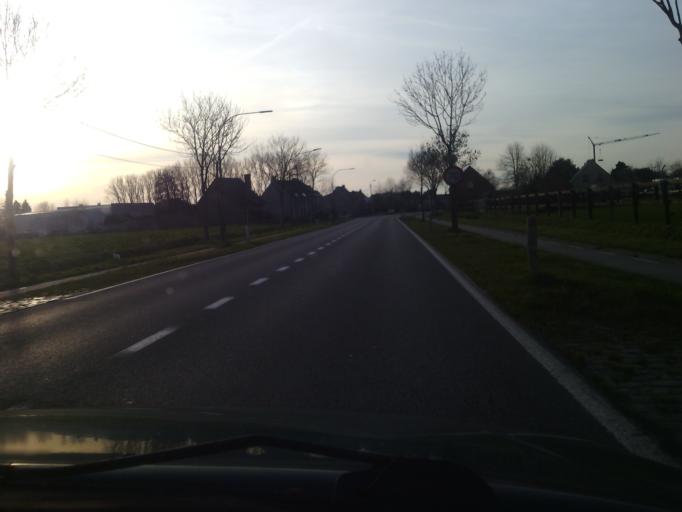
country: BE
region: Flanders
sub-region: Provincie Oost-Vlaanderen
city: Wetteren
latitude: 51.0403
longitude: 3.8992
